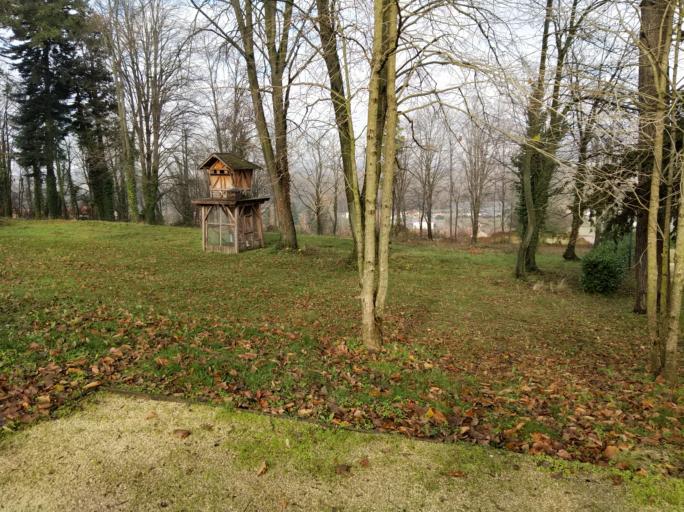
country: FR
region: Rhone-Alpes
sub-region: Departement de la Drome
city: Saint-Sorlin-en-Valloire
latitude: 45.2907
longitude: 4.9910
